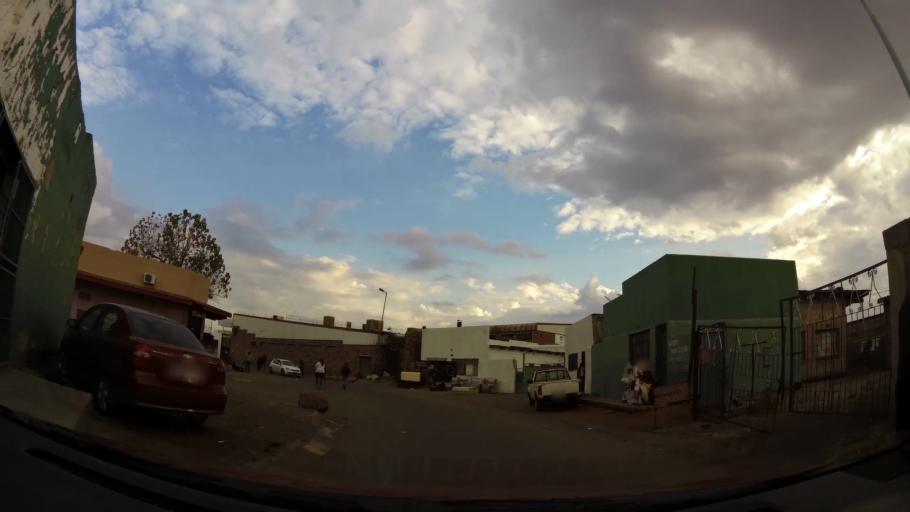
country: ZA
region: Gauteng
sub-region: City of Johannesburg Metropolitan Municipality
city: Soweto
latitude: -26.2440
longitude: 27.8201
